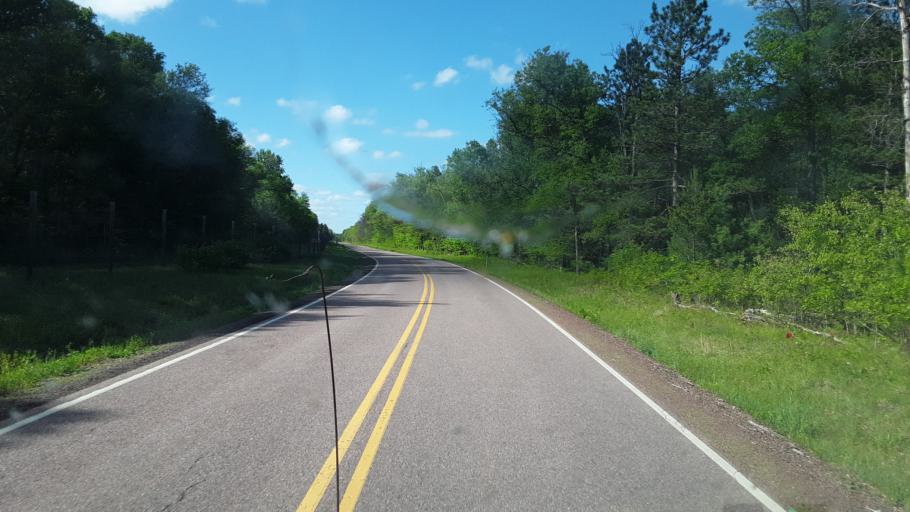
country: US
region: Wisconsin
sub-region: Wood County
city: Nekoosa
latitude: 44.3551
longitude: -90.1305
